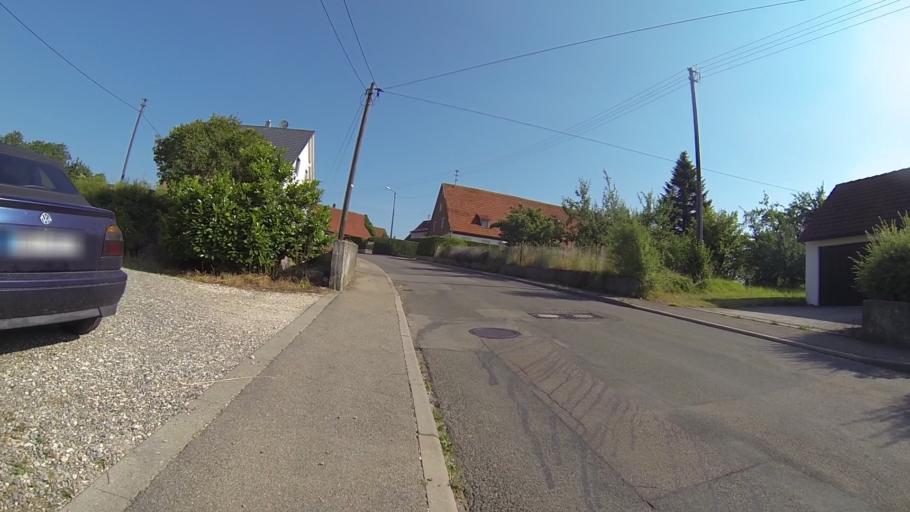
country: DE
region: Baden-Wuerttemberg
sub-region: Regierungsbezirk Stuttgart
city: Konigsbronn
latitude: 48.7428
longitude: 10.1461
